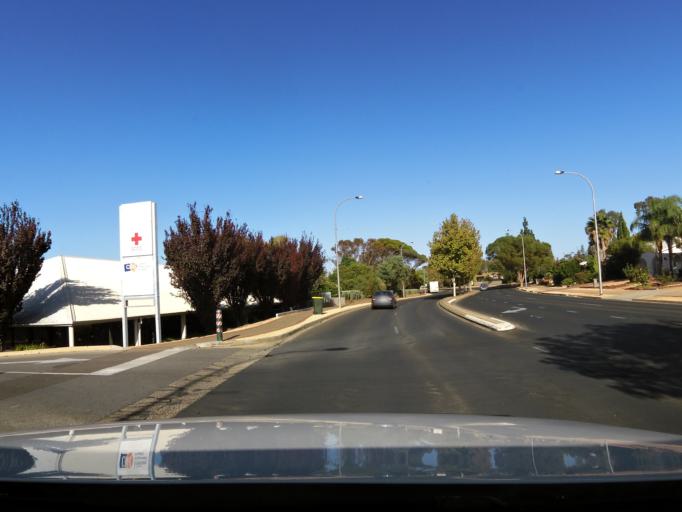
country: AU
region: South Australia
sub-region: Berri and Barmera
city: Berri
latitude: -34.2807
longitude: 140.6076
